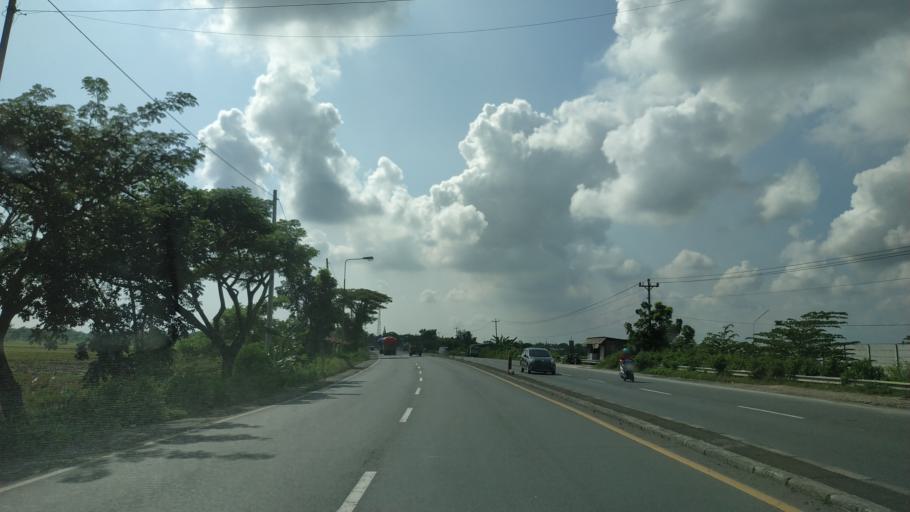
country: ID
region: Central Java
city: Wiradesa
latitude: -6.8883
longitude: 109.5783
